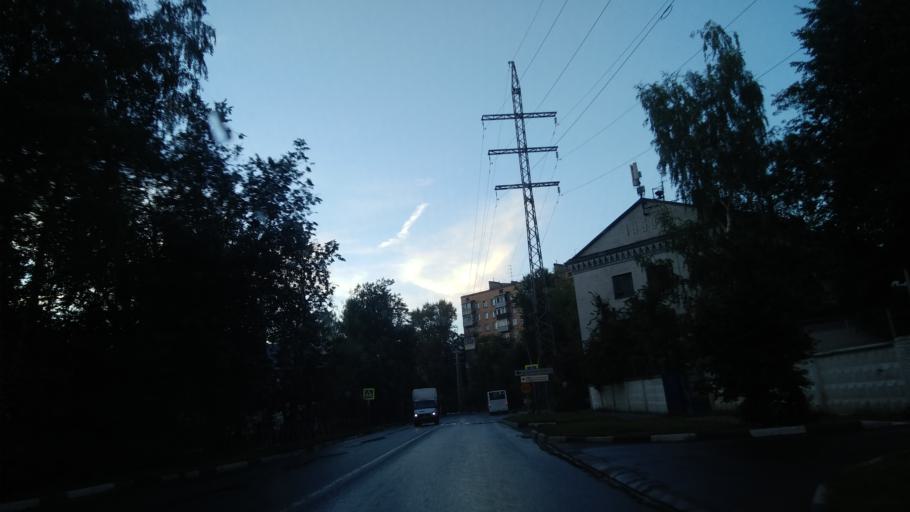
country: RU
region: Moskovskaya
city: Pushkino
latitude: 56.0083
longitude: 37.8422
